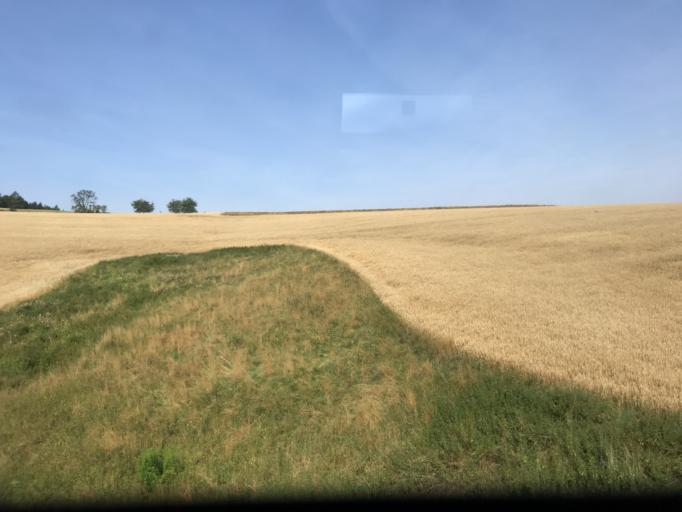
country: CZ
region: Central Bohemia
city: Votice
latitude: 49.5892
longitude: 14.5856
